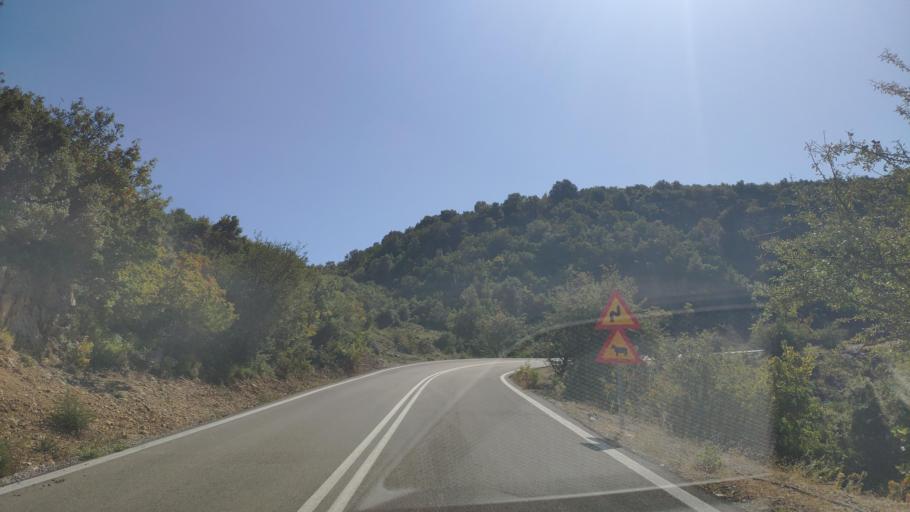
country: GR
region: West Greece
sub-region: Nomos Aitolias kai Akarnanias
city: Sardinia
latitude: 38.9249
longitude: 21.4189
